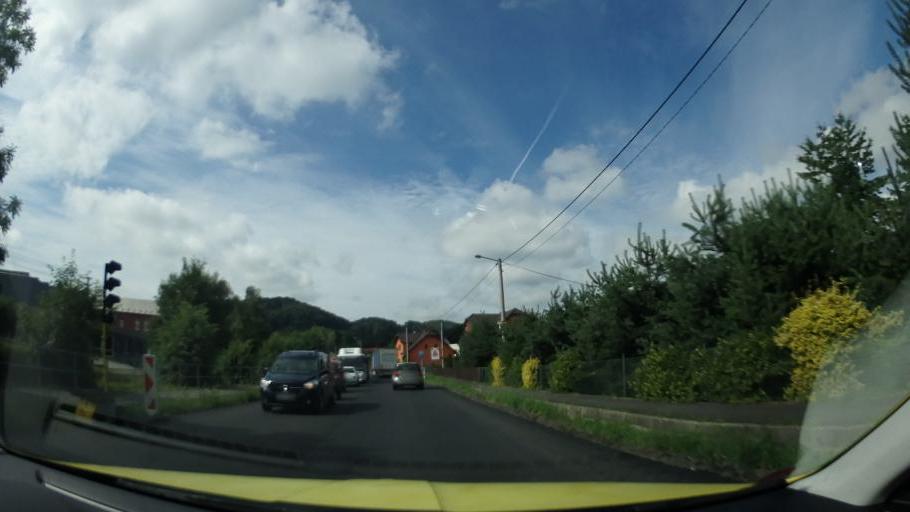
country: CZ
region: Moravskoslezsky
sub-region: Okres Novy Jicin
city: Novy Jicin
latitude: 49.5763
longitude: 18.0219
